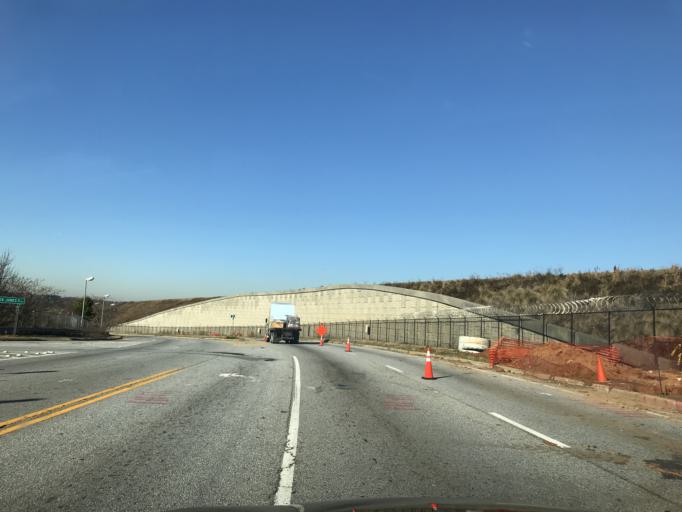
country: US
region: Georgia
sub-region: Fulton County
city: Hapeville
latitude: 33.6193
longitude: -84.4186
